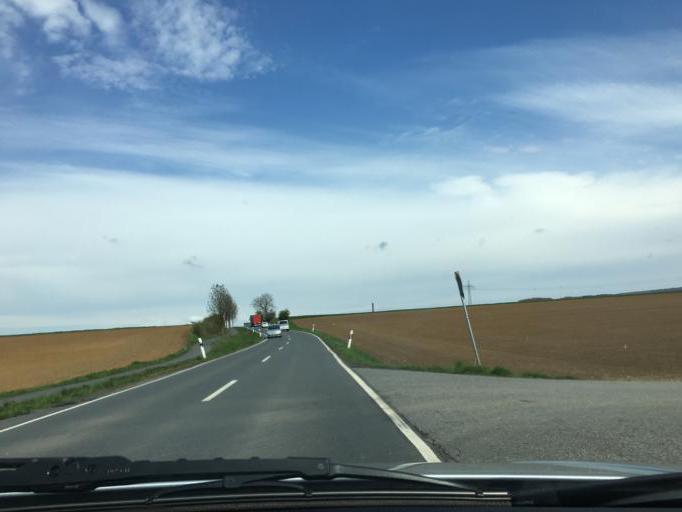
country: DE
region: Hesse
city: Gross-Umstadt
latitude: 49.8505
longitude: 8.9137
